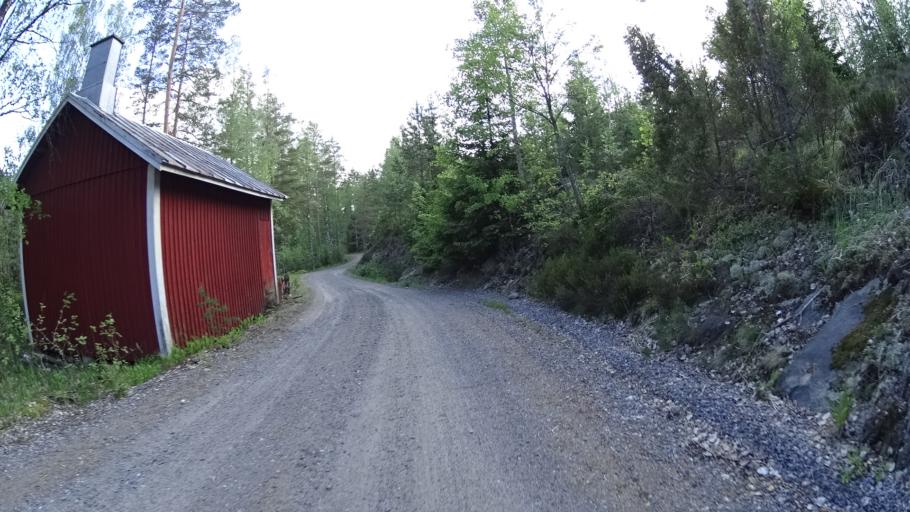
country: FI
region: Varsinais-Suomi
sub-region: Salo
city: Kisko
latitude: 60.1649
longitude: 23.4910
